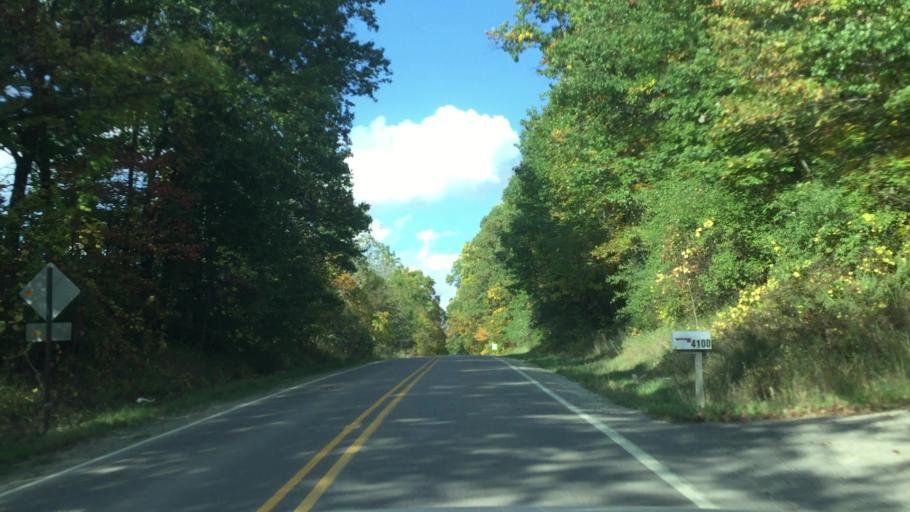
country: US
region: Michigan
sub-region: Oakland County
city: Milford
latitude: 42.6661
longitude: -83.7014
